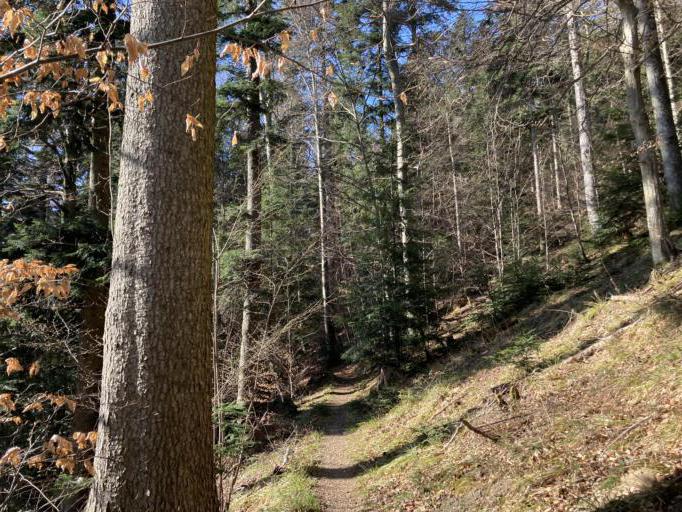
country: DE
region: Baden-Wuerttemberg
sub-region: Freiburg Region
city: Glottertal
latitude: 48.0605
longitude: 7.9618
